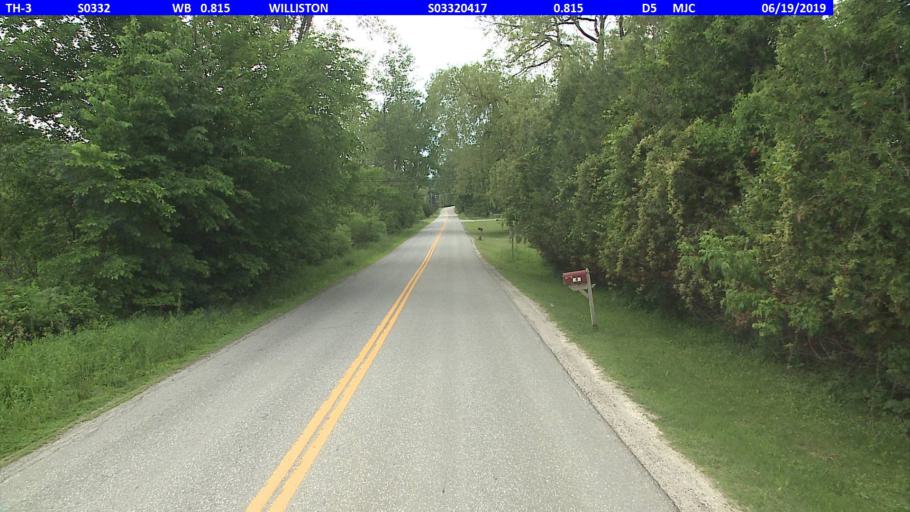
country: US
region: Vermont
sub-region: Chittenden County
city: Williston
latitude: 44.4225
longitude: -73.1074
